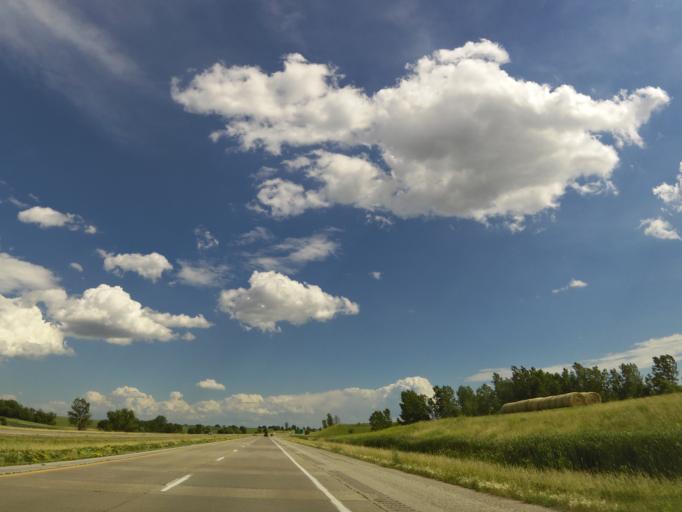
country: US
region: Iowa
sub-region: Washington County
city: Washington
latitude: 41.3099
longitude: -91.5421
